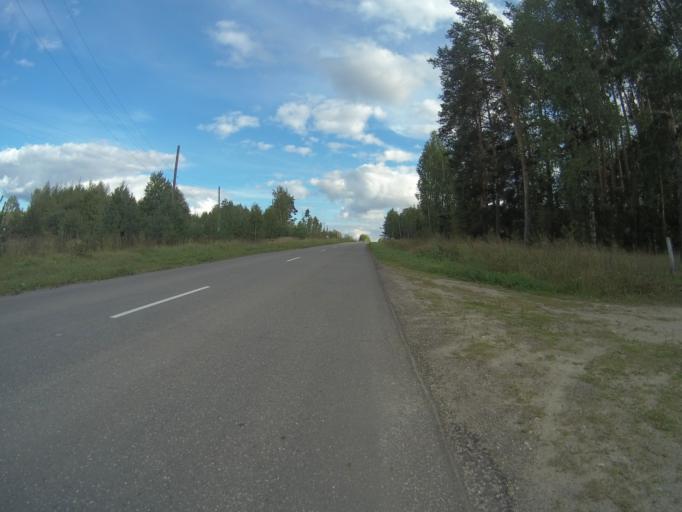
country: RU
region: Vladimir
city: Sudogda
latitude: 56.0613
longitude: 40.8122
